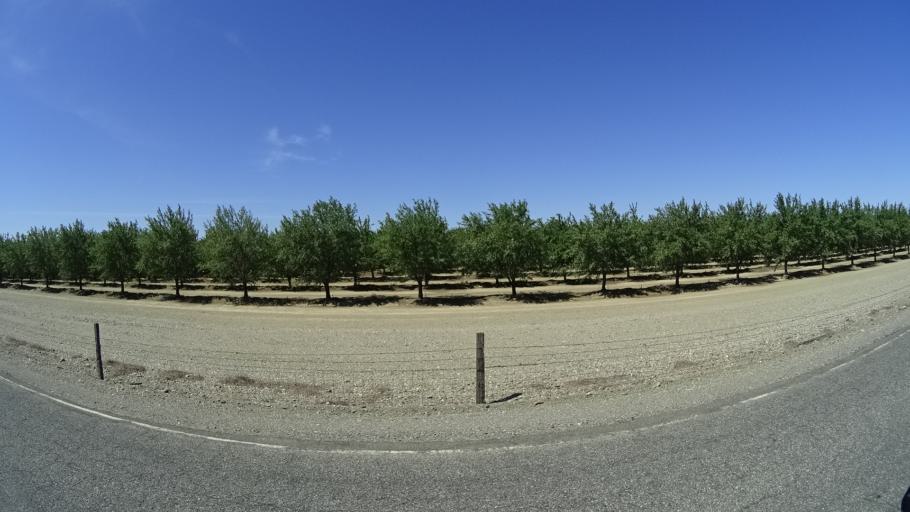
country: US
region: California
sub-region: Glenn County
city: Orland
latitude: 39.6553
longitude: -122.1784
